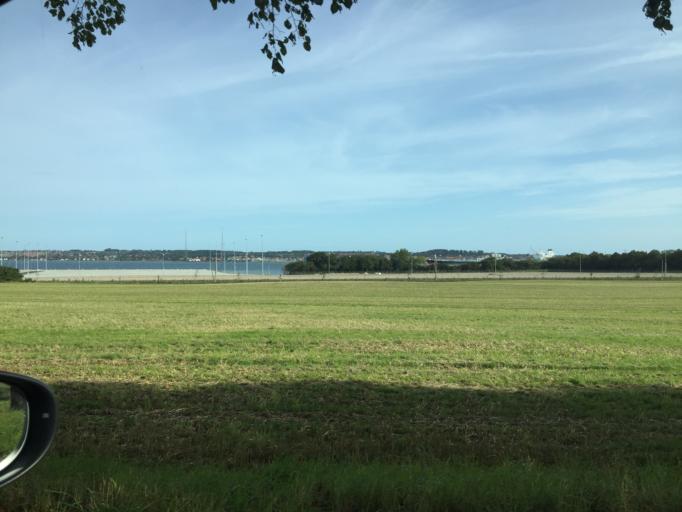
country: DK
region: Zealand
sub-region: Kalundborg Kommune
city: Kalundborg
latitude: 55.6573
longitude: 11.0650
